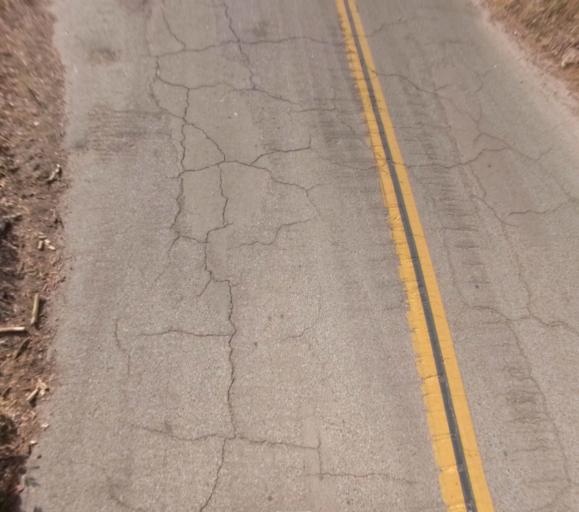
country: US
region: California
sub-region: Madera County
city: Oakhurst
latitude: 37.2507
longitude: -119.5195
